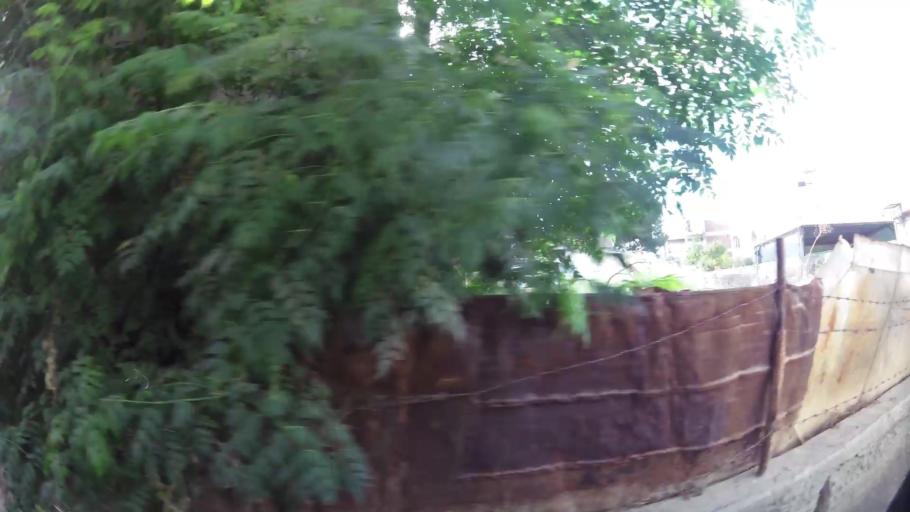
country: CY
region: Lefkosia
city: Nicosia
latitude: 35.1961
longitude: 33.3544
